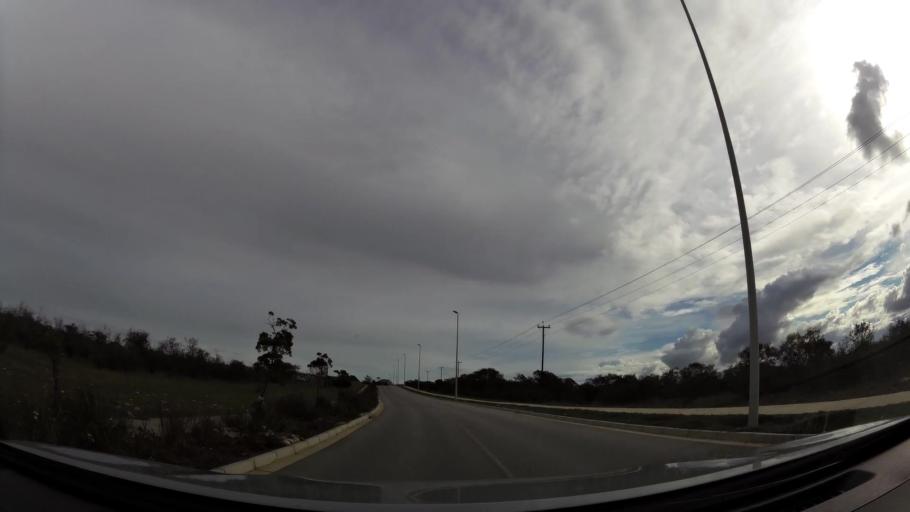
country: ZA
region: Eastern Cape
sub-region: Nelson Mandela Bay Metropolitan Municipality
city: Port Elizabeth
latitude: -33.9302
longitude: 25.4937
